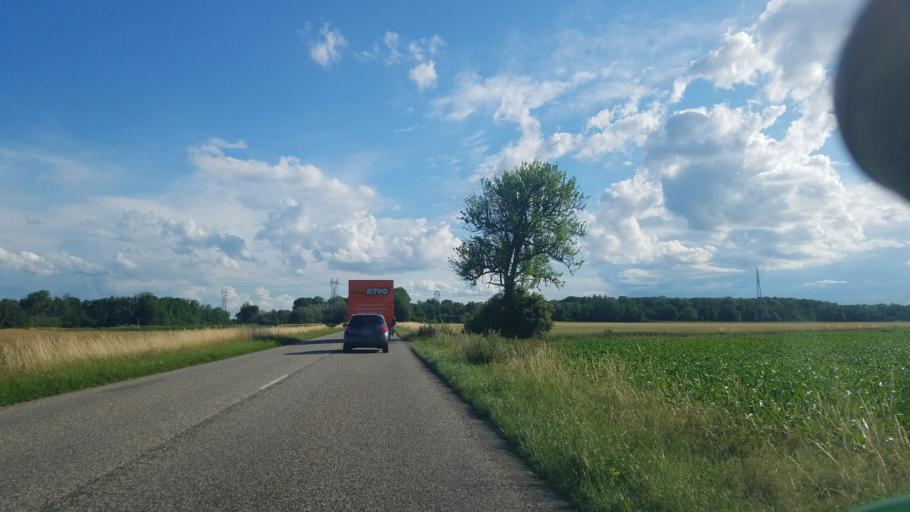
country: FR
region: Alsace
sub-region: Departement du Bas-Rhin
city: Herrlisheim
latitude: 48.7139
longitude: 7.8965
